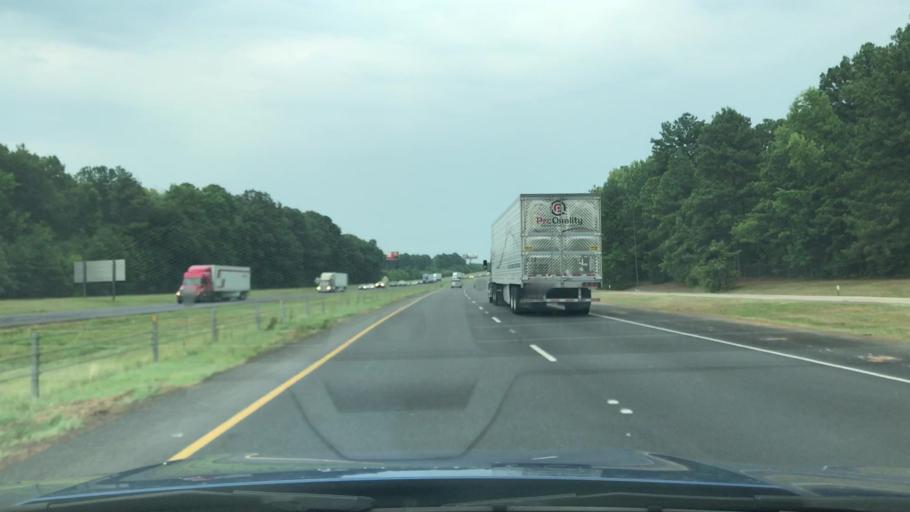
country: US
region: Louisiana
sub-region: Caddo Parish
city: Greenwood
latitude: 32.4514
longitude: -93.9992
